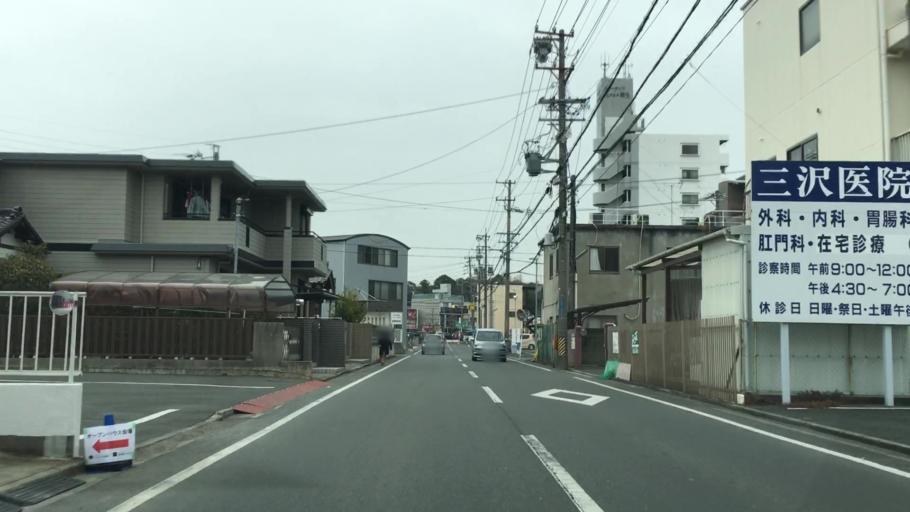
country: JP
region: Aichi
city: Toyohashi
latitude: 34.7550
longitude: 137.3913
